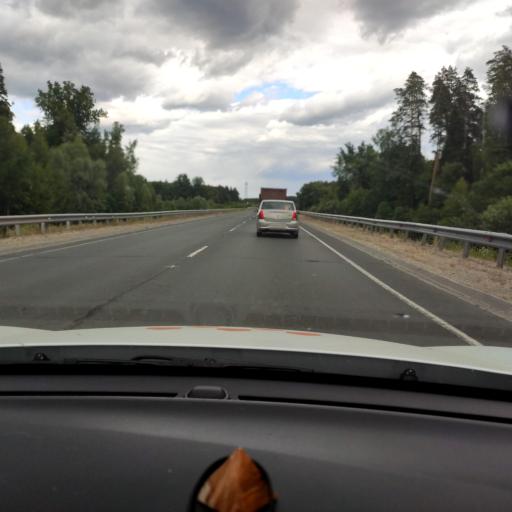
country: RU
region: Mariy-El
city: Yoshkar-Ola
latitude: 56.5421
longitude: 47.9648
